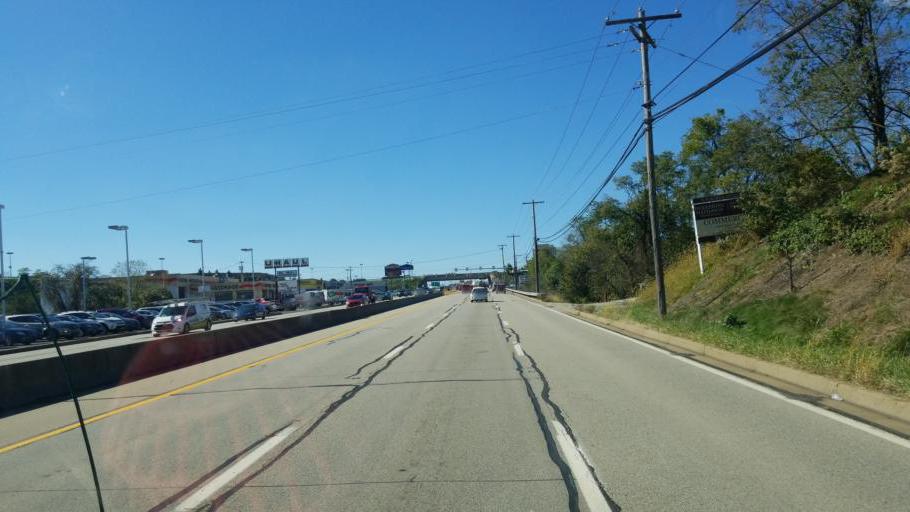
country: US
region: Pennsylvania
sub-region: Westmoreland County
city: Greensburg
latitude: 40.3029
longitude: -79.5031
